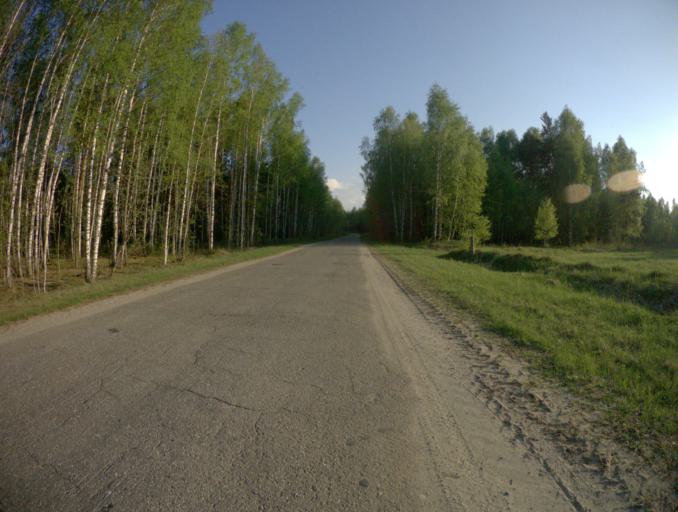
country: RU
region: Vladimir
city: Vyazniki
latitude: 56.3571
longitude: 42.1359
